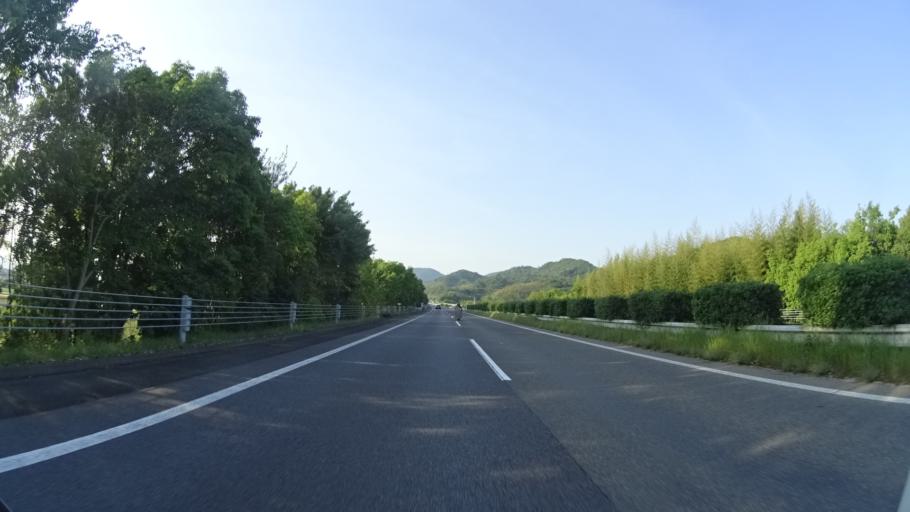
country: JP
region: Kagawa
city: Kan'onjicho
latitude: 34.1720
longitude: 133.7333
